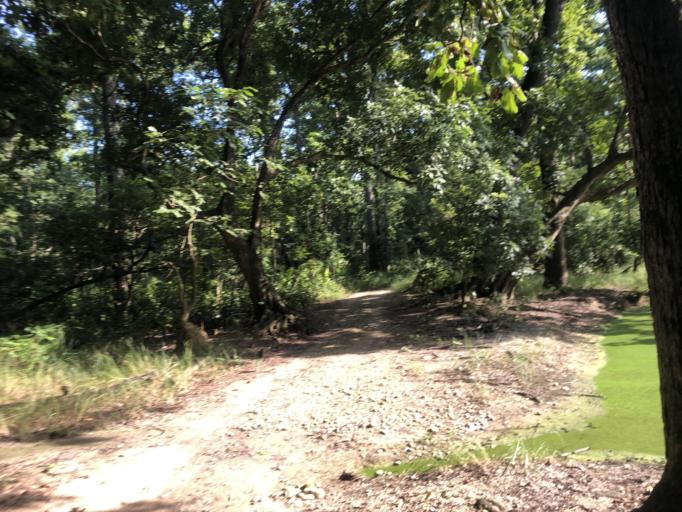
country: NP
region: Far Western
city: Tikapur
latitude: 28.5383
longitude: 81.2856
